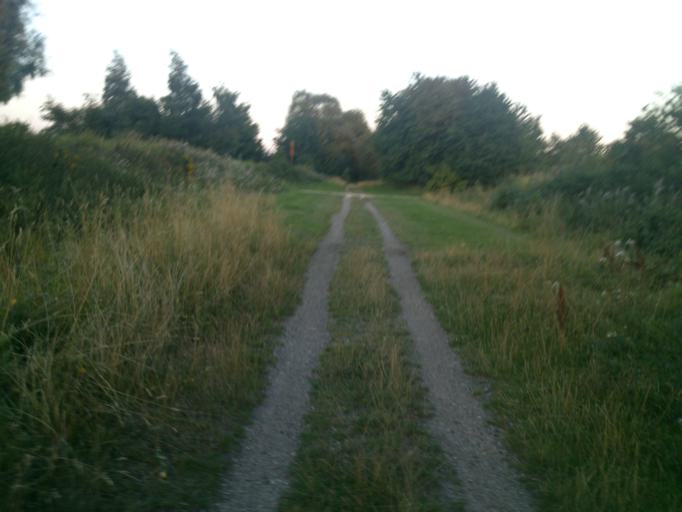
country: DK
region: South Denmark
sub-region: Fredericia Kommune
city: Fredericia
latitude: 55.5750
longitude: 9.7146
